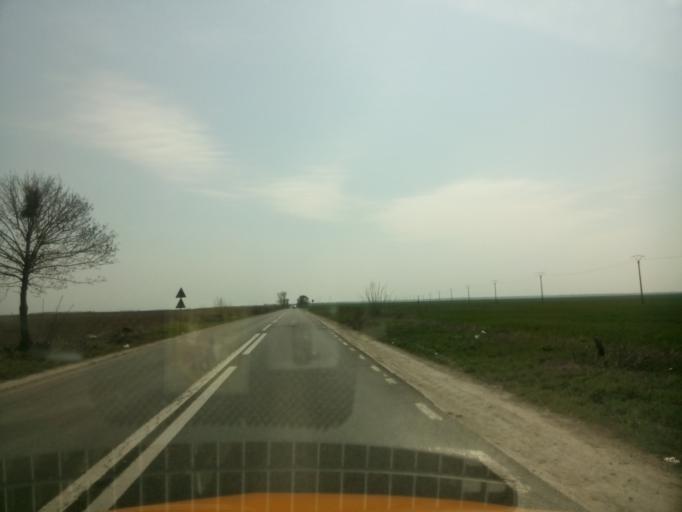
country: RO
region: Giurgiu
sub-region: Comuna Herasti
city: Herasti
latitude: 44.2481
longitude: 26.3739
